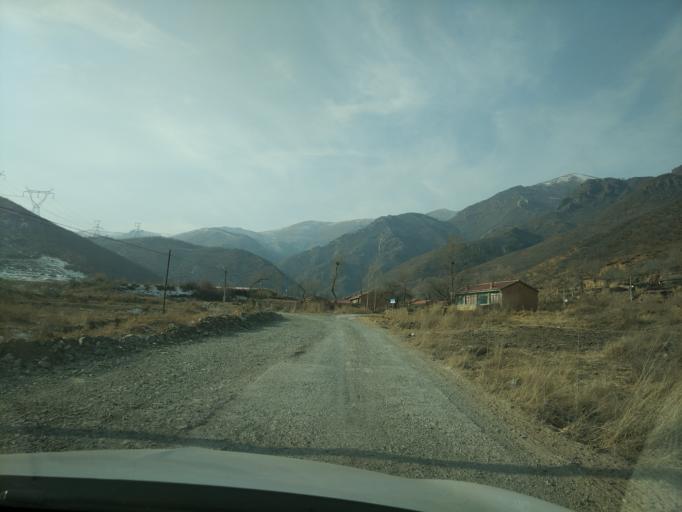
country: CN
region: Hebei
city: Xiwanzi
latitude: 40.8139
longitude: 115.4619
